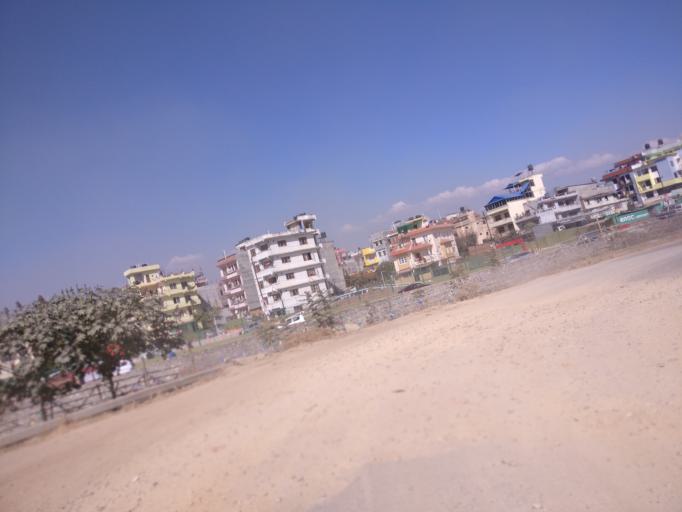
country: NP
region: Central Region
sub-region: Bagmati Zone
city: Patan
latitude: 27.6786
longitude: 85.3343
